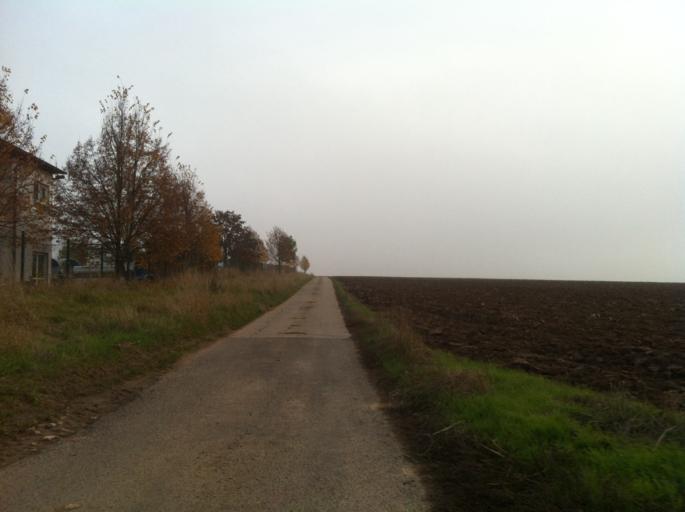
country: DE
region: Rheinland-Pfalz
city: Essenheim
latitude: 49.9567
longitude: 8.1436
